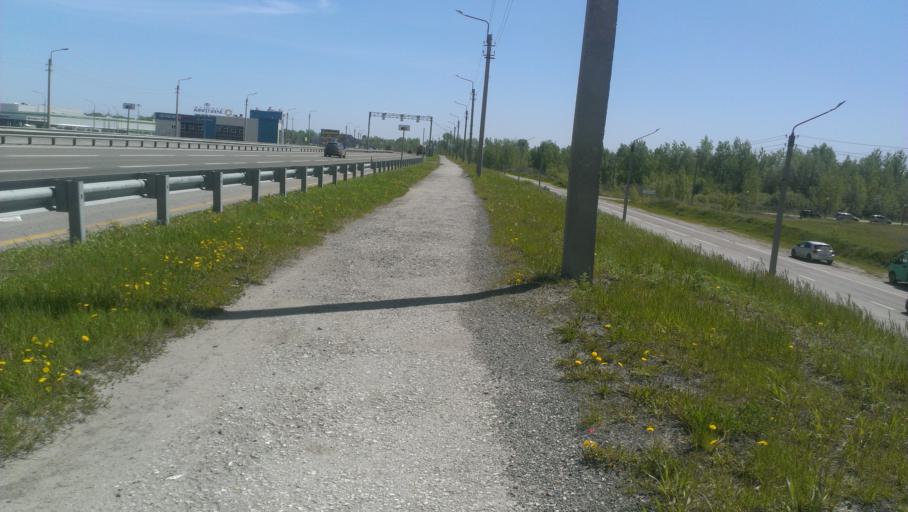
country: RU
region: Altai Krai
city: Zaton
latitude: 53.3174
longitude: 83.8208
